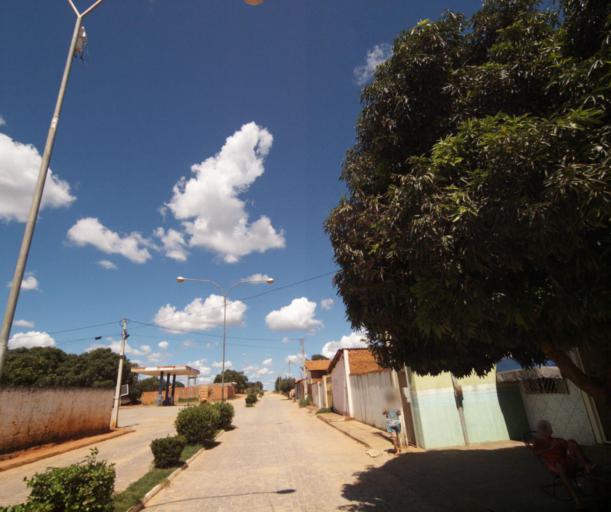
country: BR
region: Bahia
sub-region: Carinhanha
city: Carinhanha
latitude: -14.2116
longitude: -44.2788
